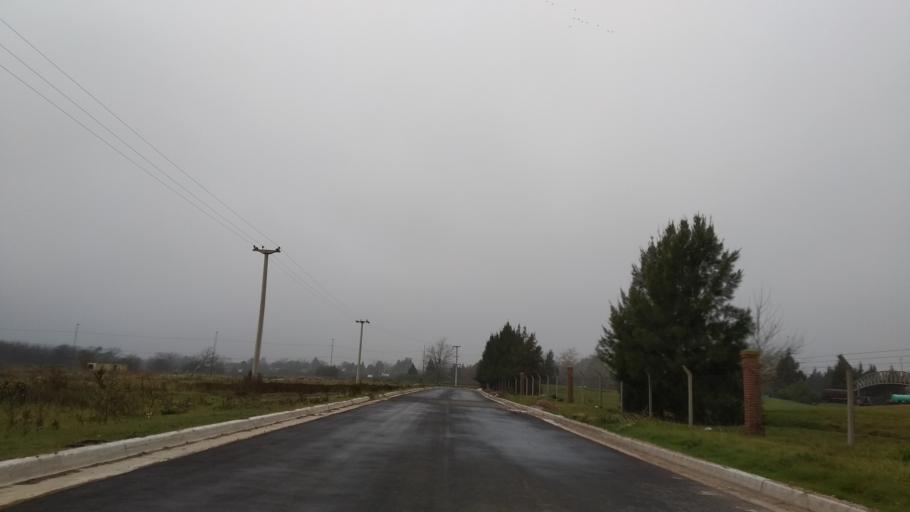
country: AR
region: Santa Fe
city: Funes
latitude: -32.9358
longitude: -60.7646
